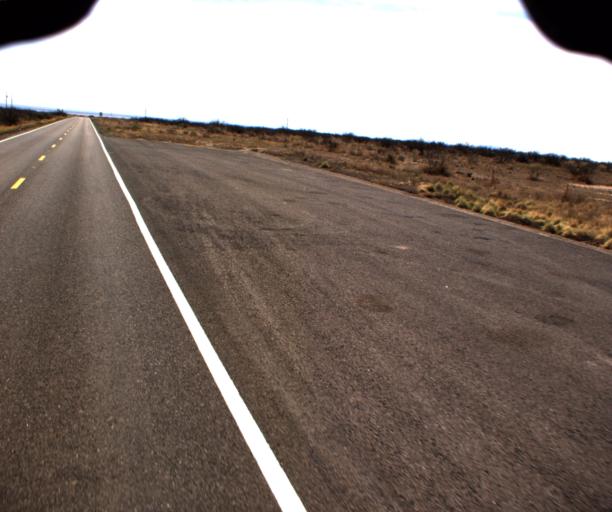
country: US
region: Arizona
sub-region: Cochise County
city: Willcox
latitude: 32.1398
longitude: -109.9225
